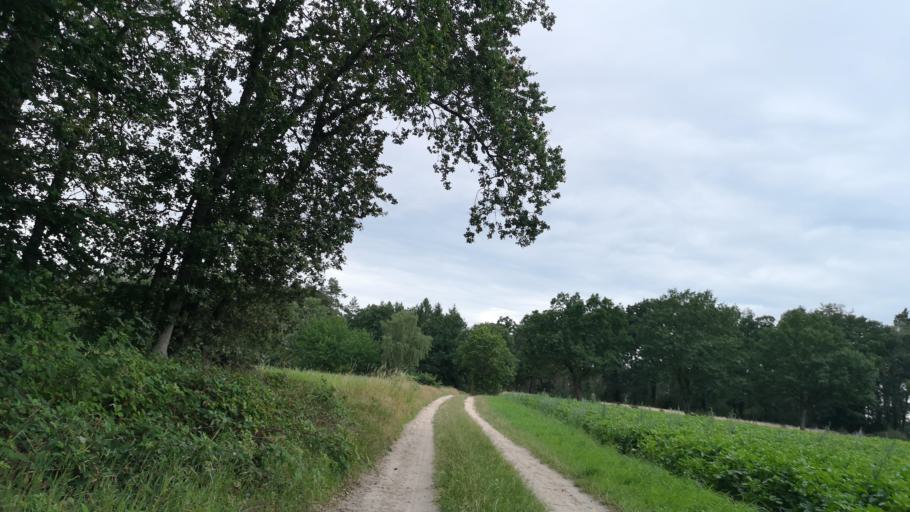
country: DE
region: Lower Saxony
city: Thomasburg
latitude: 53.2103
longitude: 10.6952
